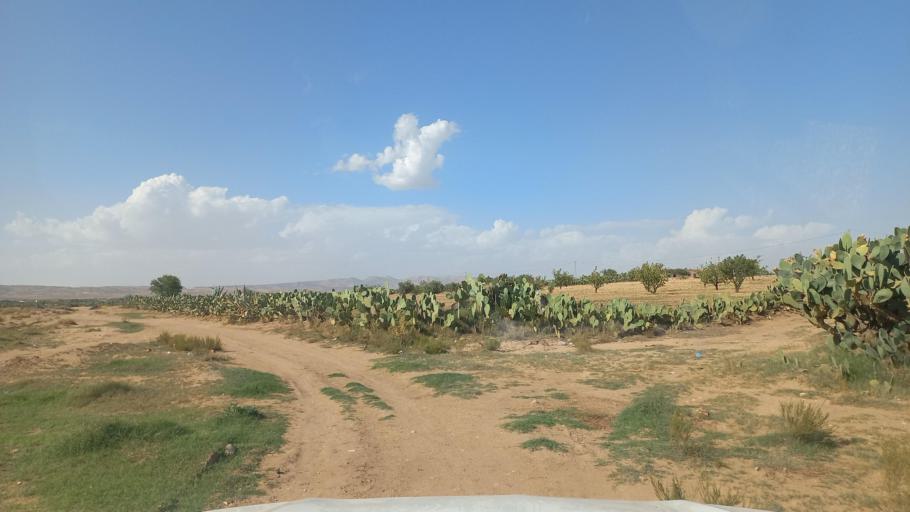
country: TN
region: Al Qasrayn
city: Sbiba
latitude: 35.3098
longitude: 9.0336
